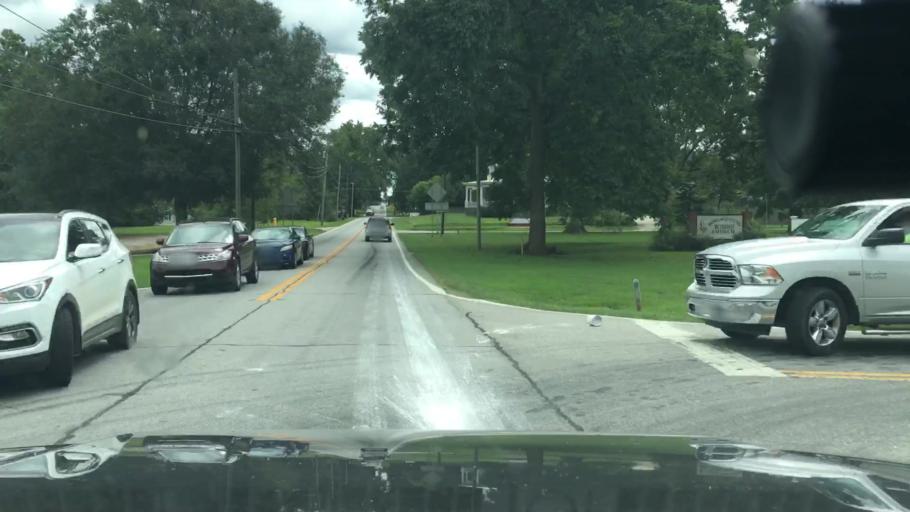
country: US
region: Georgia
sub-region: Coweta County
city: East Newnan
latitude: 33.2868
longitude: -84.7677
